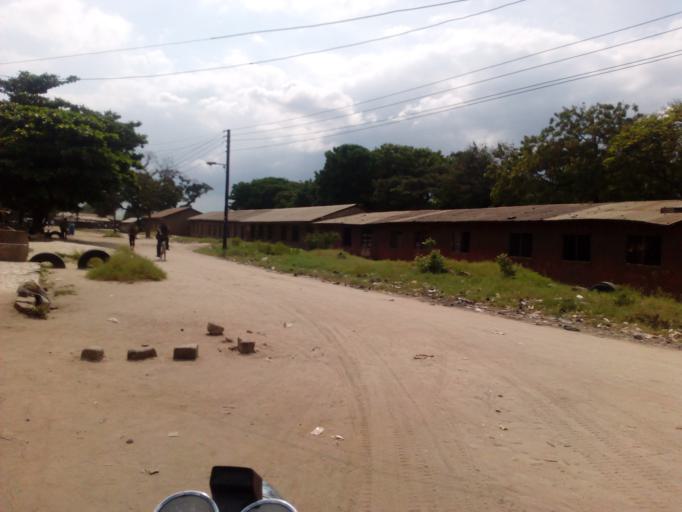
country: TZ
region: Dar es Salaam
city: Dar es Salaam
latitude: -6.8556
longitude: 39.2587
